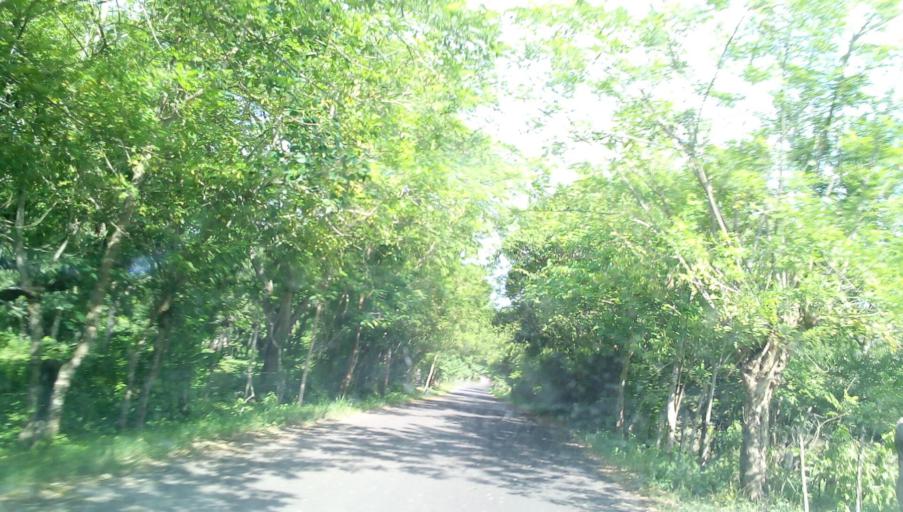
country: MX
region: Veracruz
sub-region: Citlaltepetl
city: Las Sabinas
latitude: 21.3546
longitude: -97.8981
